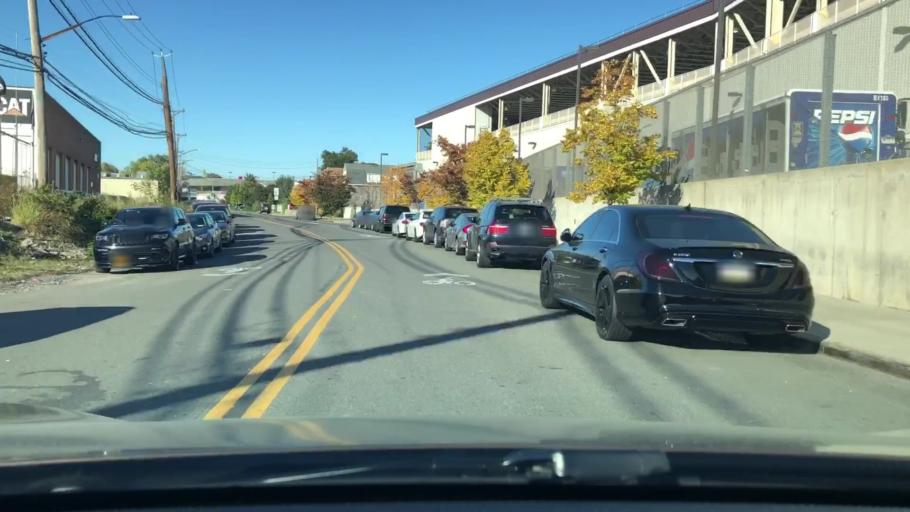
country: US
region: New York
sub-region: Bronx
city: The Bronx
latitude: 40.8192
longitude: -73.8380
